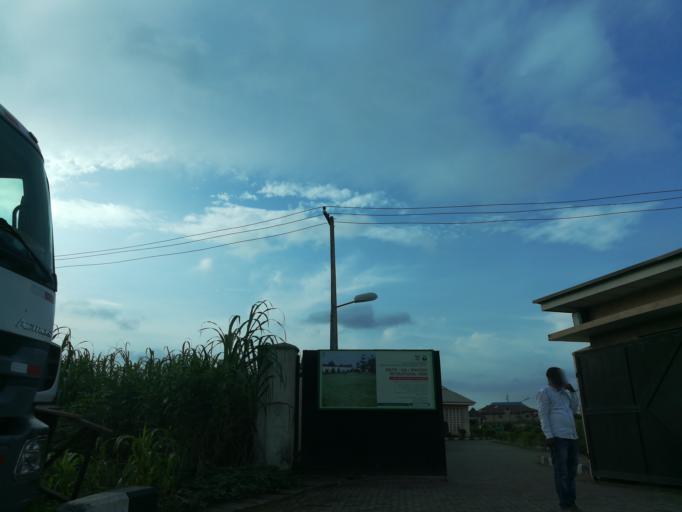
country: NG
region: Lagos
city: Ebute Ikorodu
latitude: 6.6034
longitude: 3.4852
